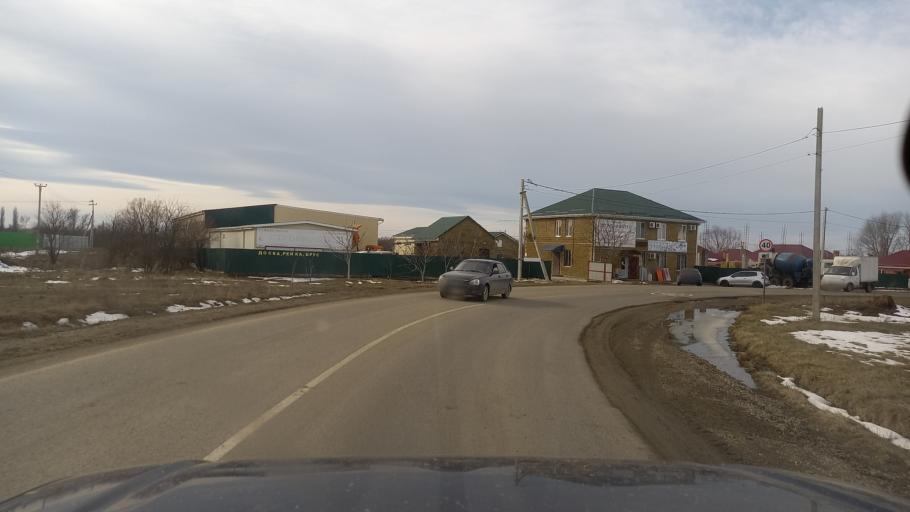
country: RU
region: Krasnodarskiy
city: Belorechensk
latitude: 44.7663
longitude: 39.9072
